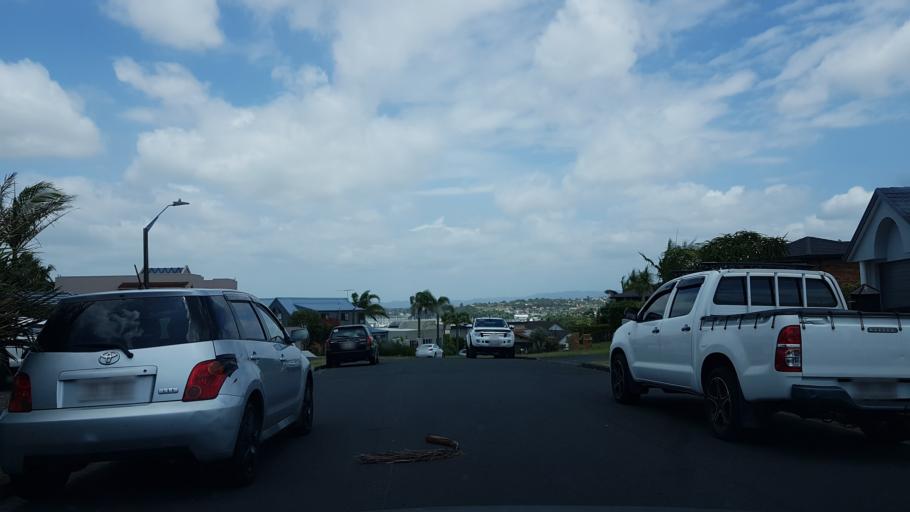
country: NZ
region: Auckland
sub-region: Auckland
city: Rosebank
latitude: -36.7996
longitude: 174.6498
